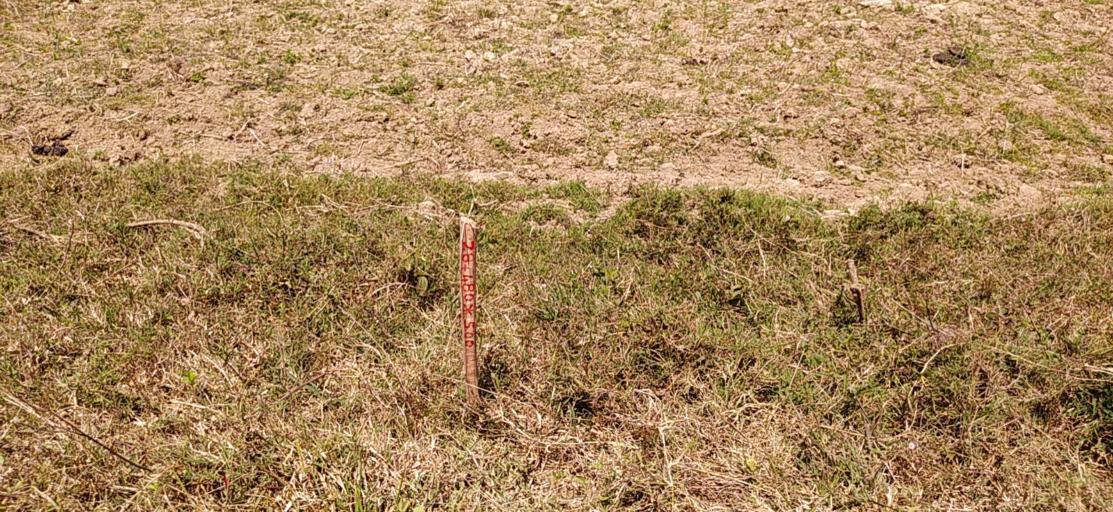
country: MG
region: Alaotra Mangoro
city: Moramanga
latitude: -18.7066
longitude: 48.2712
